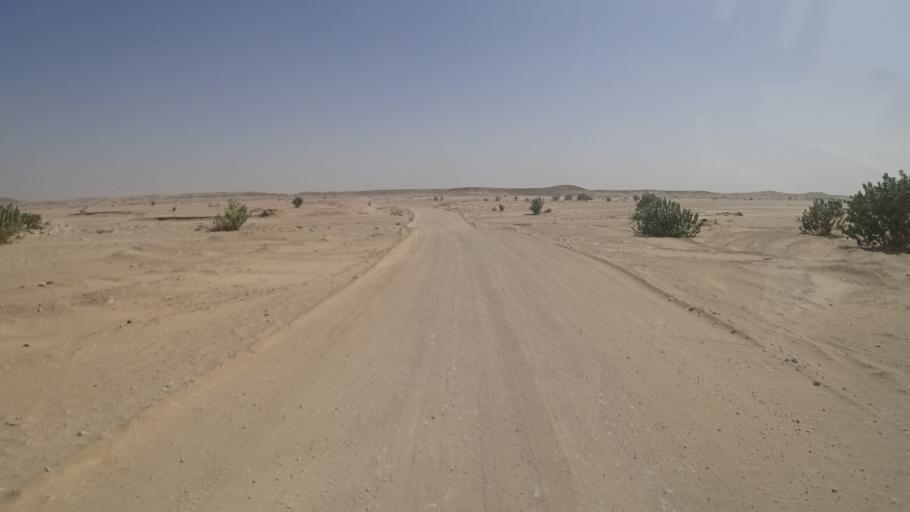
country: YE
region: Al Mahrah
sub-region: Shahan
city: Shihan as Sufla
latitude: 17.8770
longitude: 52.6052
